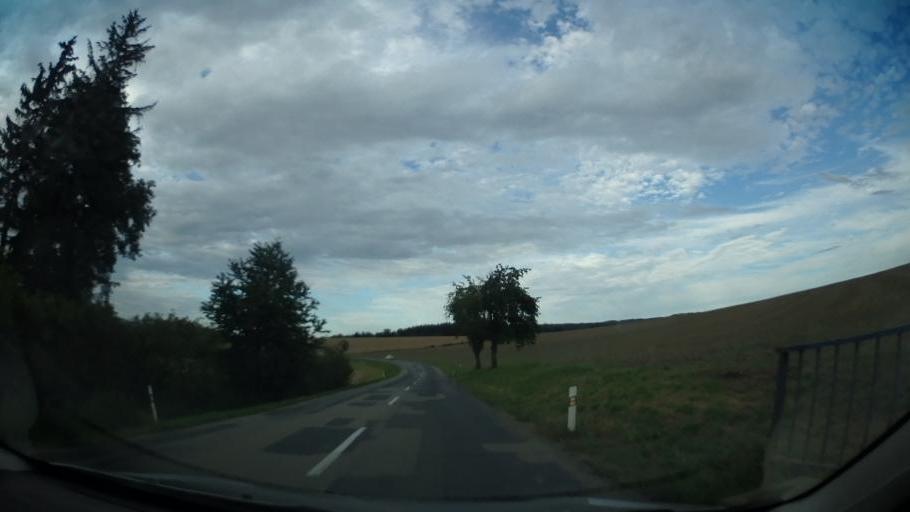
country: CZ
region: South Moravian
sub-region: Okres Blansko
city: Boskovice
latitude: 49.5003
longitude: 16.6673
